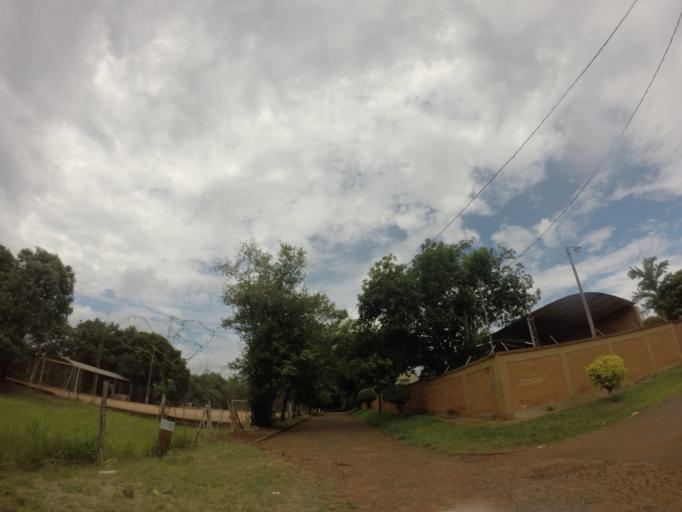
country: PY
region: Alto Parana
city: Ciudad del Este
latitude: -25.4151
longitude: -54.6317
